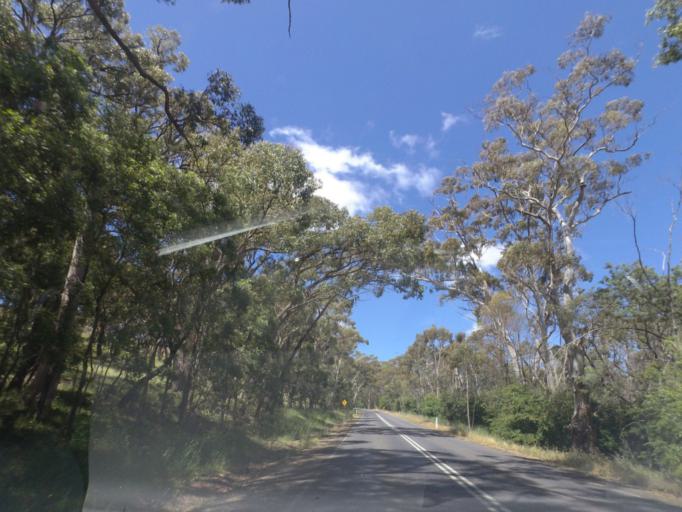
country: AU
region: Victoria
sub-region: Mount Alexander
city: Castlemaine
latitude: -37.2904
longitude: 144.2643
